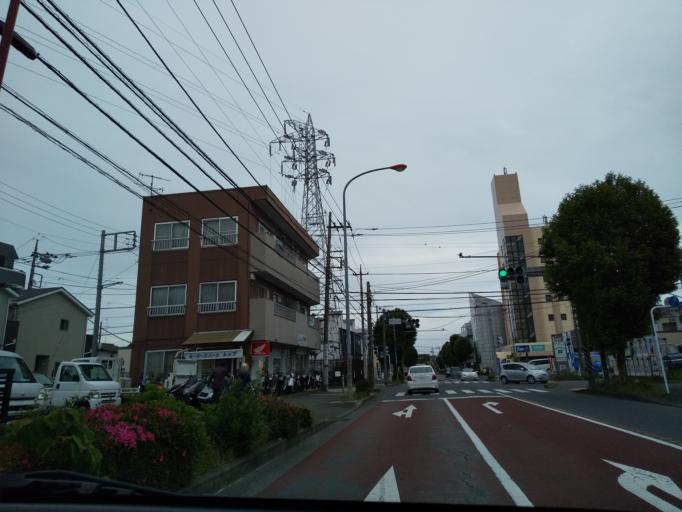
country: JP
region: Kanagawa
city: Zama
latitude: 35.5161
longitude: 139.4057
